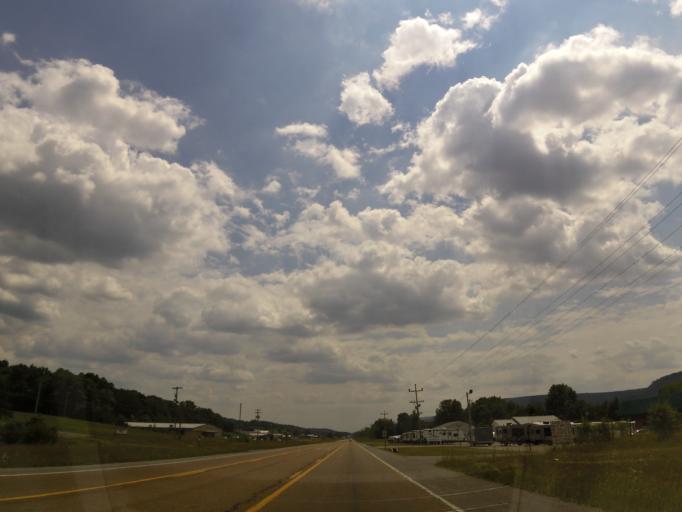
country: US
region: Tennessee
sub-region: Sequatchie County
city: Dunlap
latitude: 35.3452
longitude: -85.4086
